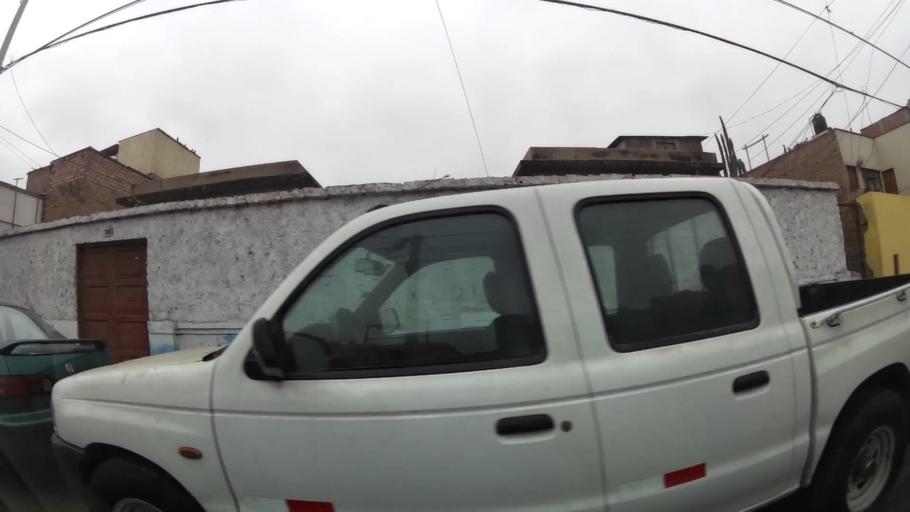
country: PE
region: Callao
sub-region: Callao
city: Callao
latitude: -12.0872
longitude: -77.0865
